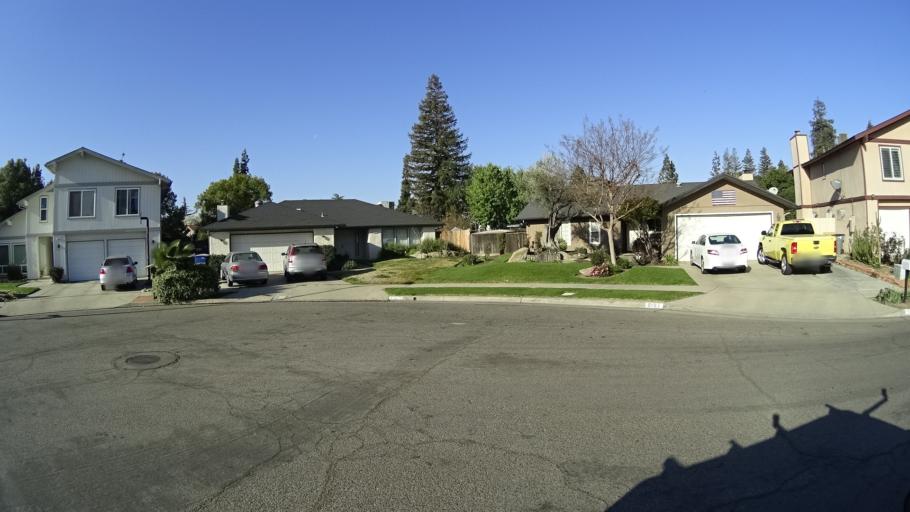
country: US
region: California
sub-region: Fresno County
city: Clovis
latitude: 36.8547
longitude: -119.7951
